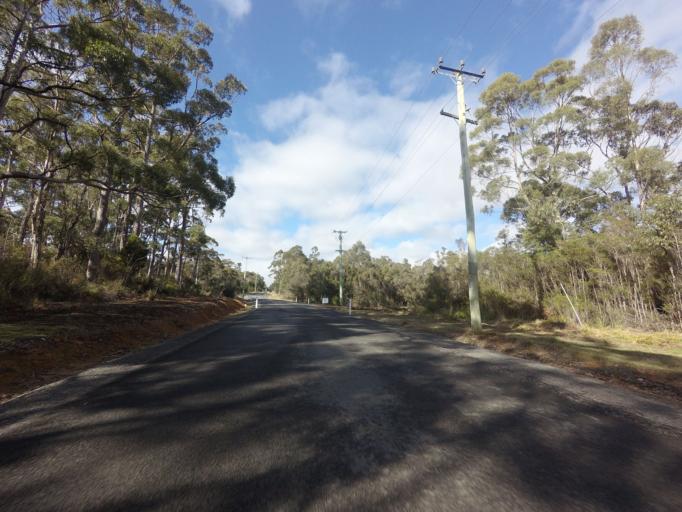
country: AU
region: Tasmania
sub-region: Huon Valley
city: Geeveston
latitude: -43.4330
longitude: 146.9035
